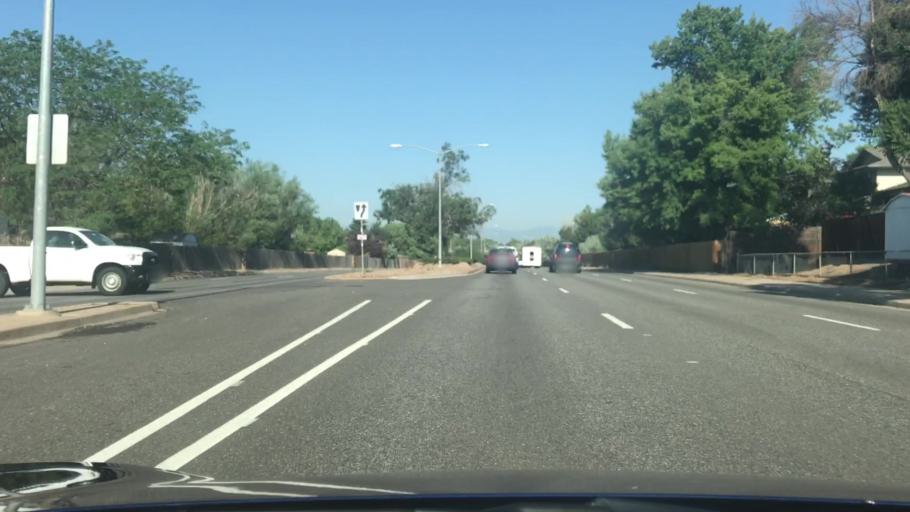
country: US
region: Colorado
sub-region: Arapahoe County
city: Dove Valley
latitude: 39.6531
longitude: -104.7872
